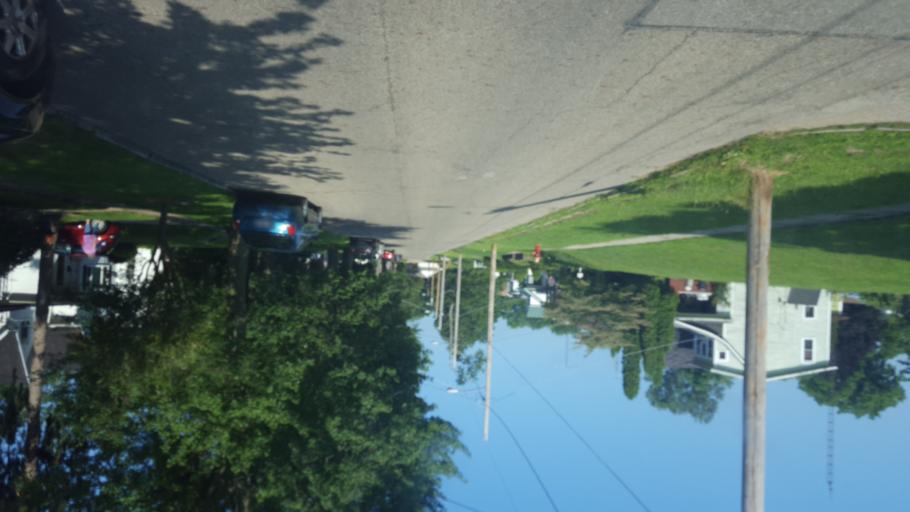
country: US
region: Ohio
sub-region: Crawford County
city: Galion
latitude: 40.7312
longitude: -82.7943
